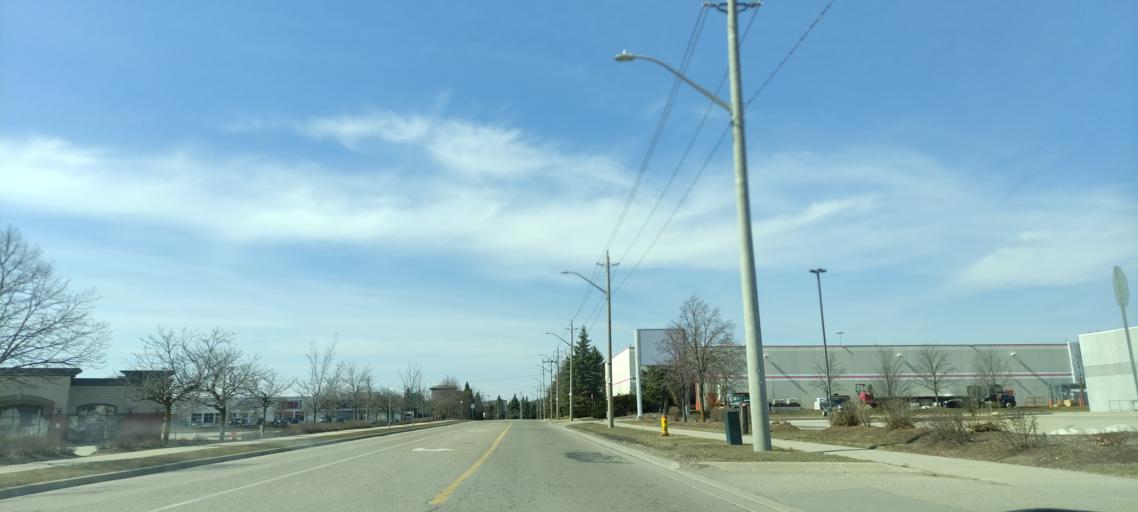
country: CA
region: Ontario
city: Cambridge
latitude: 43.4063
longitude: -80.3868
